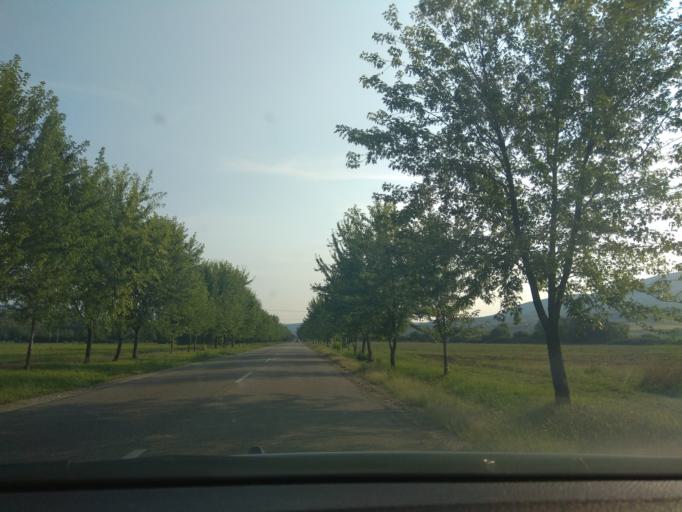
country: HU
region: Heves
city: Felsotarkany
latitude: 47.9571
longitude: 20.3949
